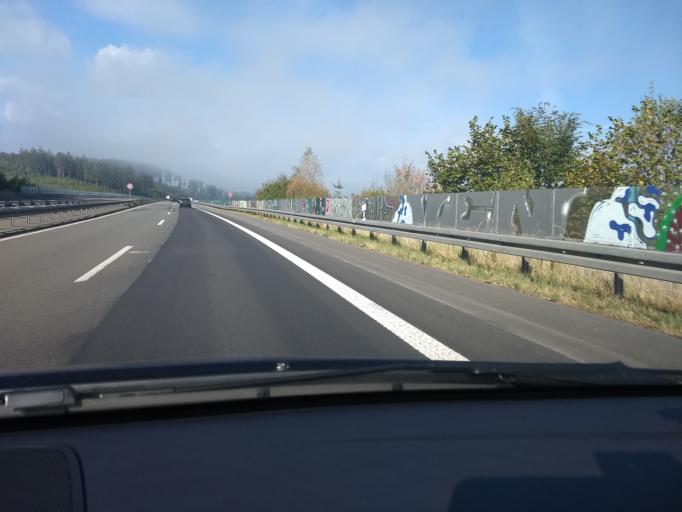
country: DE
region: North Rhine-Westphalia
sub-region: Regierungsbezirk Arnsberg
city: Arnsberg
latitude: 51.3837
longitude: 8.1386
